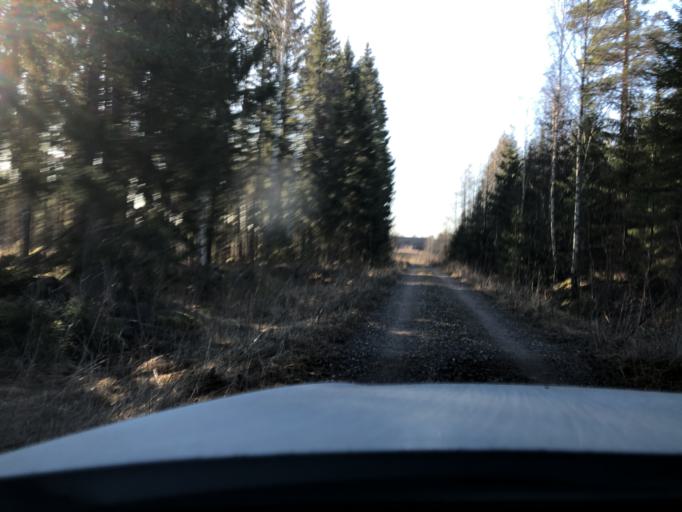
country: SE
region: Gaevleborg
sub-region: Gavle Kommun
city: Hedesunda
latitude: 60.2980
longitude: 16.8881
